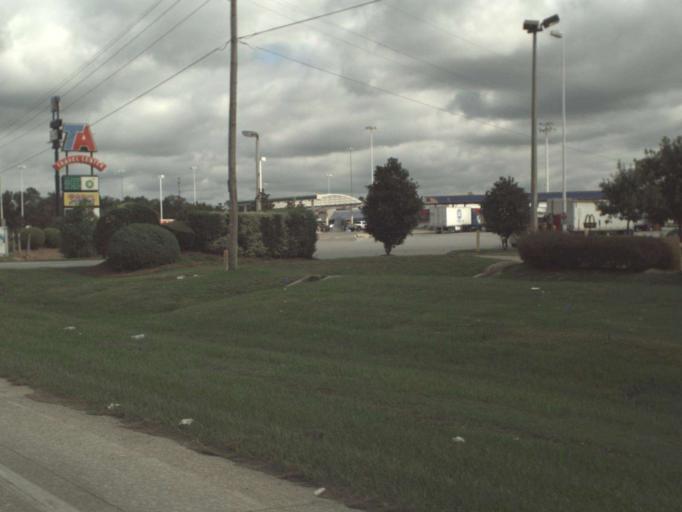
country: US
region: Florida
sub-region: Jackson County
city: Marianna
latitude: 30.7172
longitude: -85.1853
